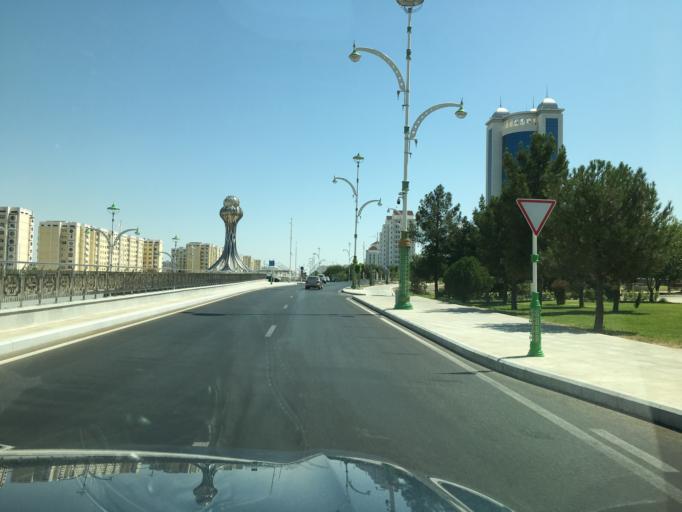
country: TM
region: Ahal
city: Ashgabat
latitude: 37.8954
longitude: 58.3863
